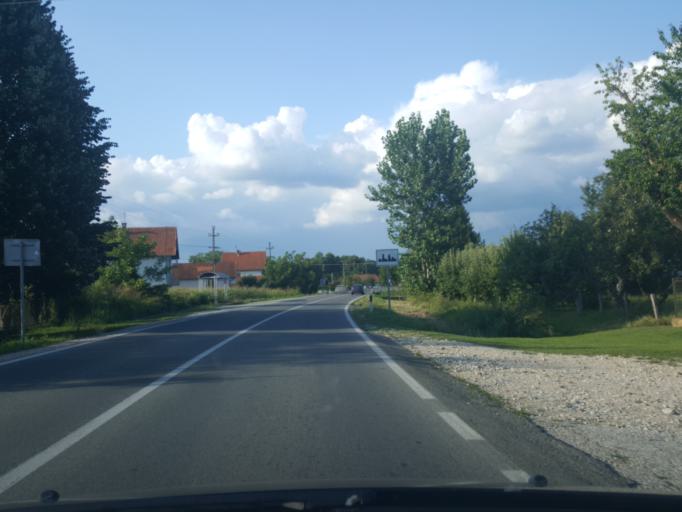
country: RS
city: Lipnicki Sor
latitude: 44.6034
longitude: 19.2544
